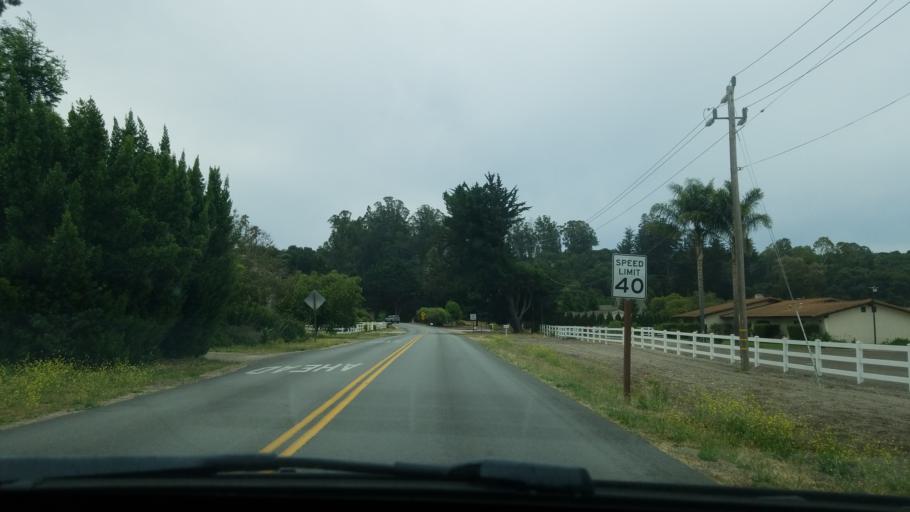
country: US
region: California
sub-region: San Luis Obispo County
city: Callender
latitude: 35.0775
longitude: -120.5428
